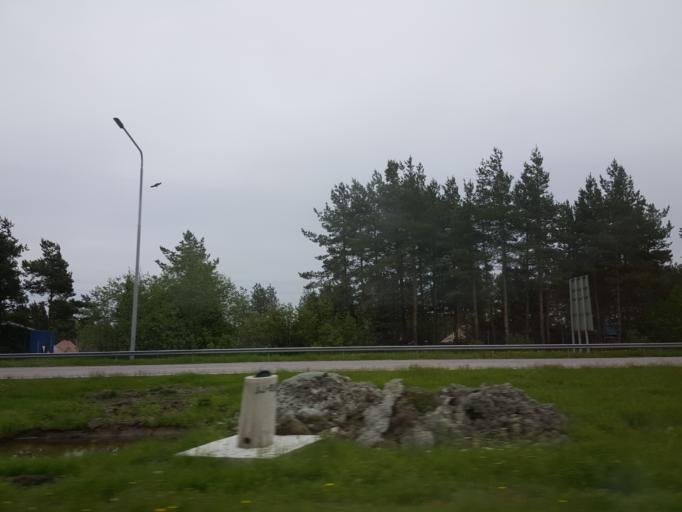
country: FI
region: Uusimaa
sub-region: Helsinki
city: Vantaa
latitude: 60.2637
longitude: 24.9670
